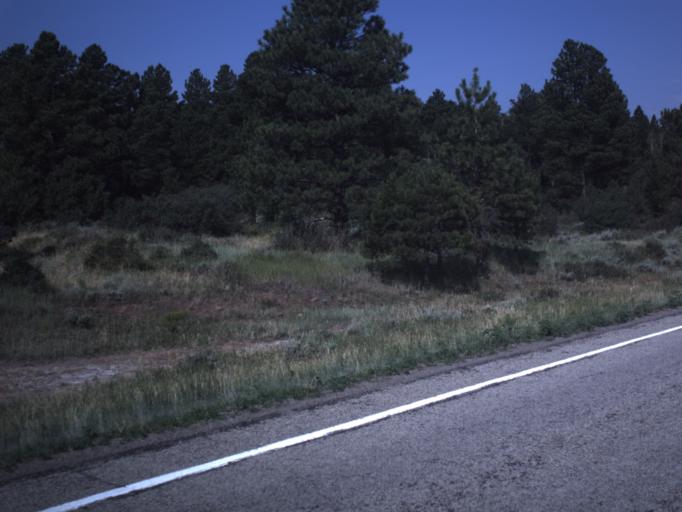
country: US
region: Utah
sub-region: Daggett County
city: Manila
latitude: 40.8665
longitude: -109.4874
